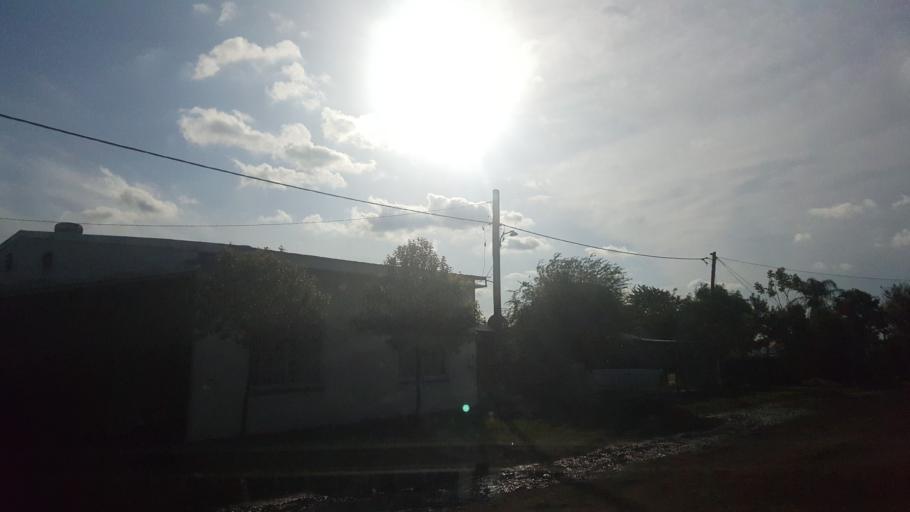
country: AR
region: Misiones
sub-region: Departamento de Candelaria
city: Candelaria
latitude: -27.5617
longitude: -55.7072
